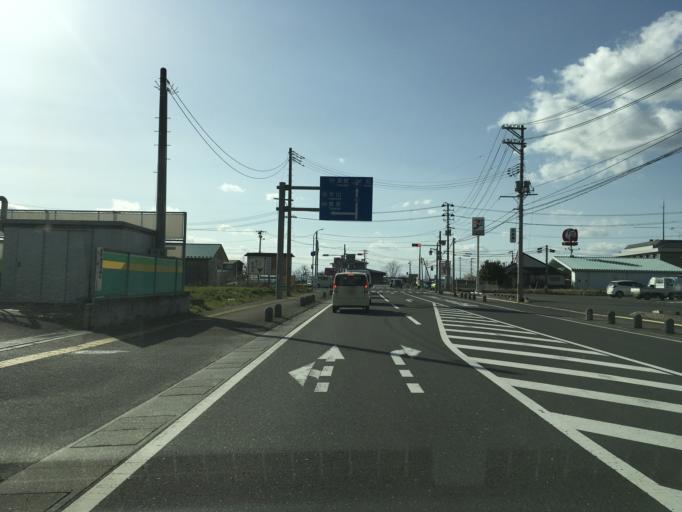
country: JP
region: Miyagi
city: Wakuya
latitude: 38.6565
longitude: 141.2748
